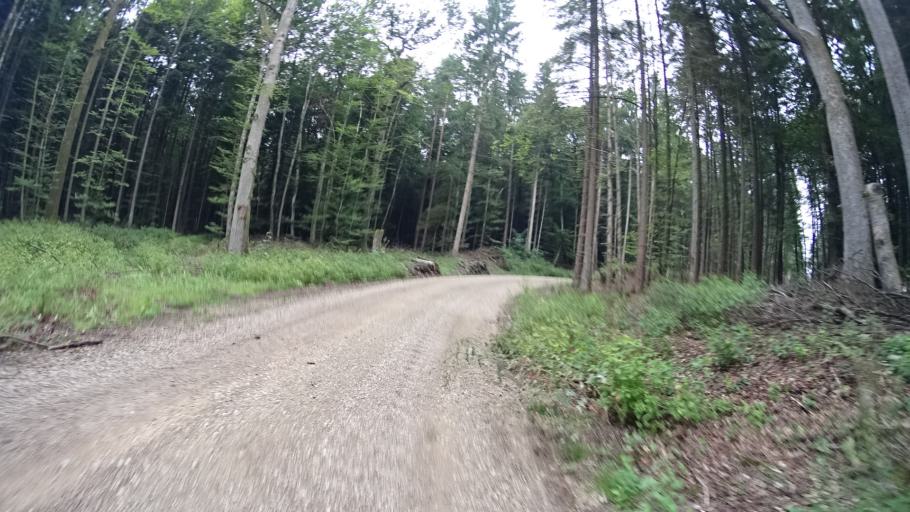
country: DE
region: Bavaria
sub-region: Upper Bavaria
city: Stammham
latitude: 48.8515
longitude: 11.4939
